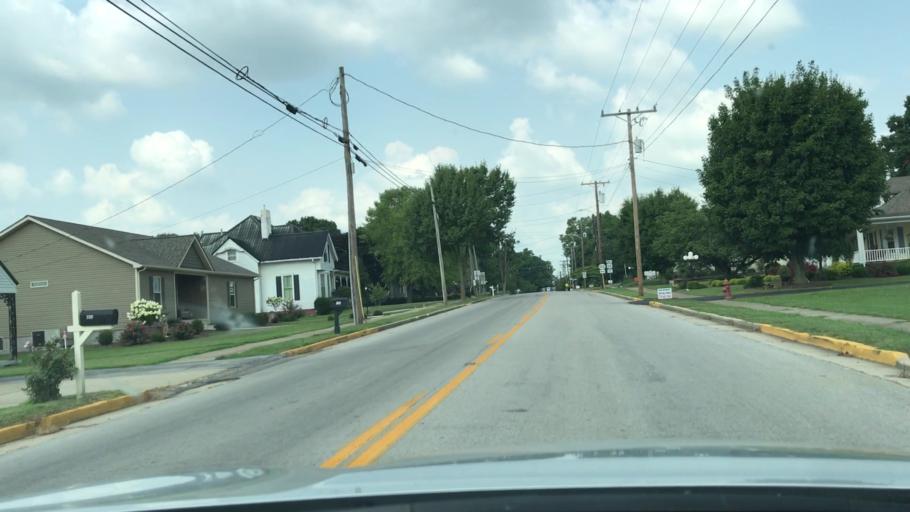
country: US
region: Kentucky
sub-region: Todd County
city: Elkton
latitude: 36.8085
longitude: -87.1466
